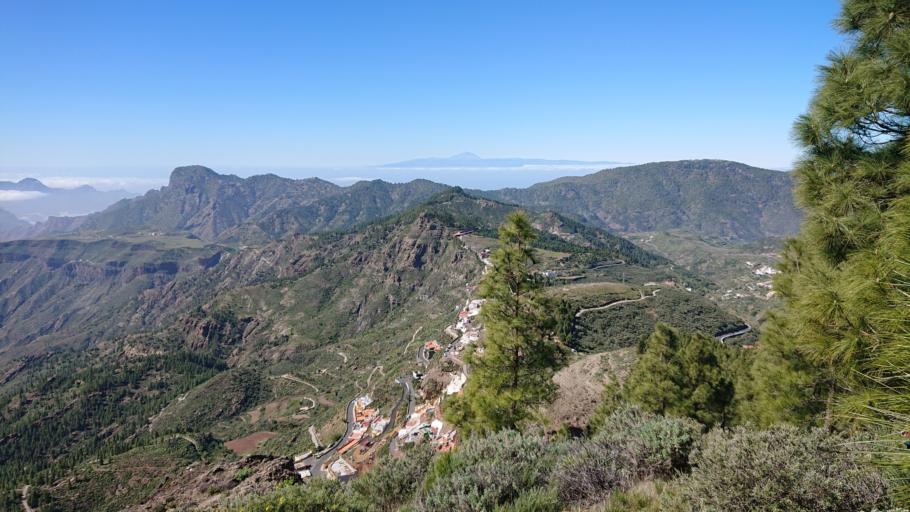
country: ES
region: Canary Islands
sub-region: Provincia de Las Palmas
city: Artenara
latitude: 28.0174
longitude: -15.6383
